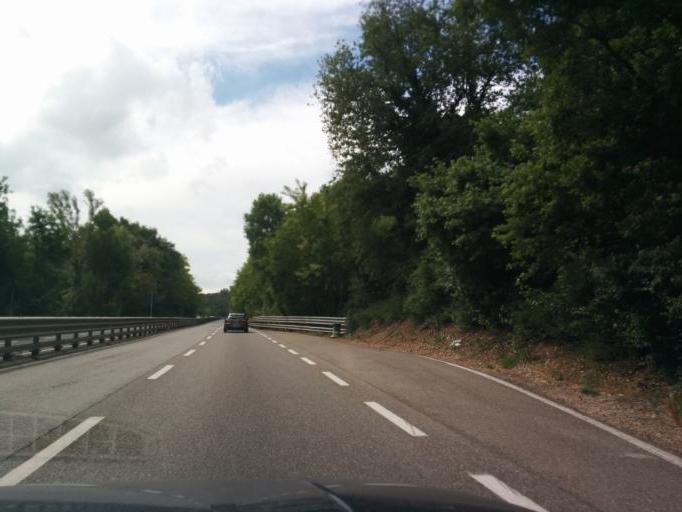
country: IT
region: Tuscany
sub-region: Province of Florence
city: Sambuca
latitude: 43.5759
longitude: 11.2049
